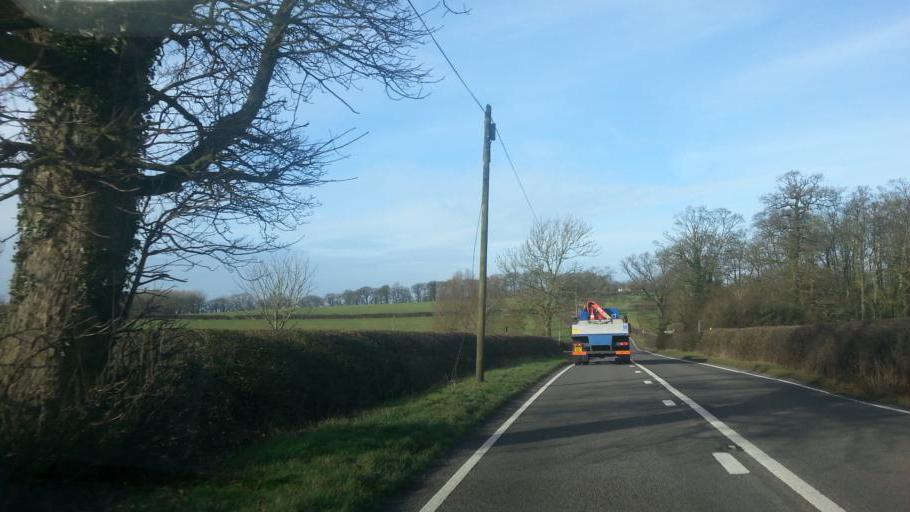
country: GB
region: England
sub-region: Leicestershire
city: Houghton on the Hill
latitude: 52.6673
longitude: -0.9301
